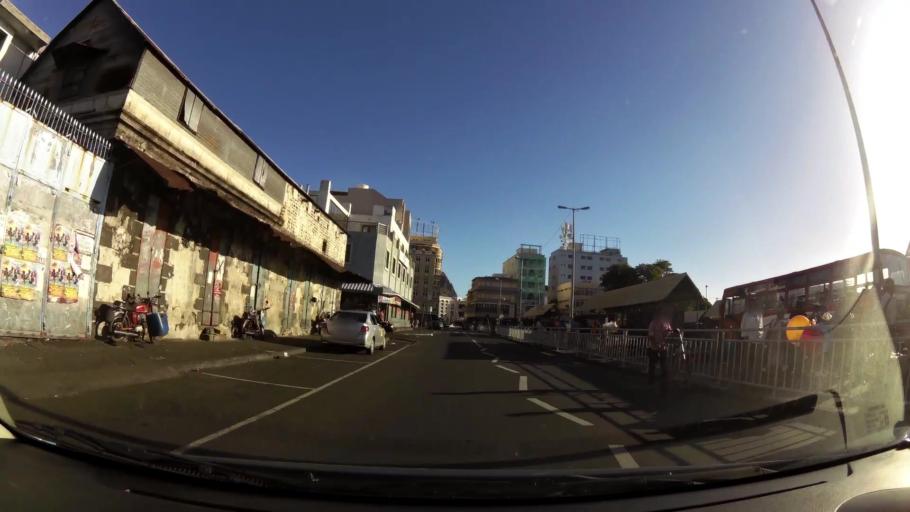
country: MU
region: Port Louis
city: Port Louis
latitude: -20.1590
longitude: 57.5043
